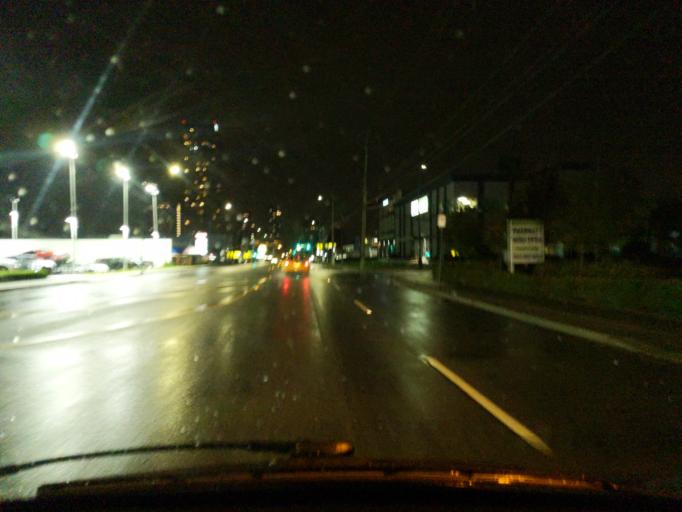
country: CA
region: British Columbia
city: New Westminster
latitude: 49.1916
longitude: -122.8391
